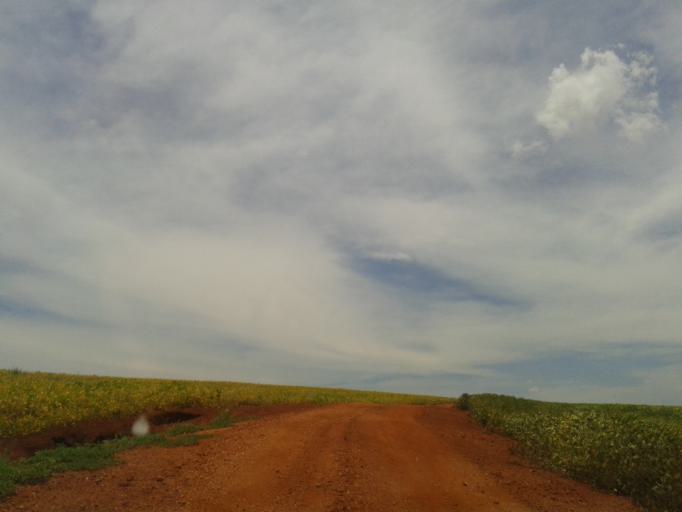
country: BR
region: Minas Gerais
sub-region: Capinopolis
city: Capinopolis
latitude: -18.6855
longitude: -49.7108
